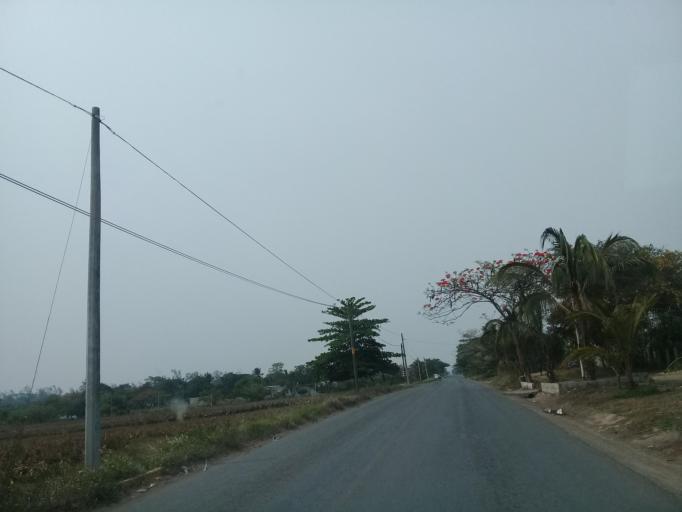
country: MX
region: Veracruz
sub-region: Medellin
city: La Laguna y Monte del Castillo
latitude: 18.9800
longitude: -96.1183
